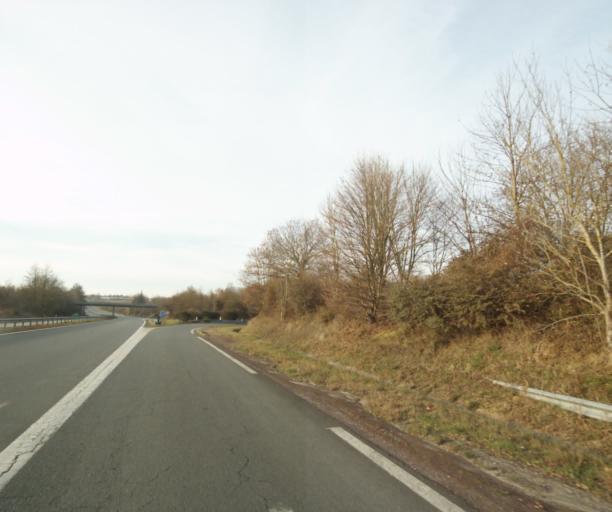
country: FR
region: Poitou-Charentes
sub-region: Departement de la Charente-Maritime
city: Saint-Porchaire
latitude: 45.8112
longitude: -0.7657
